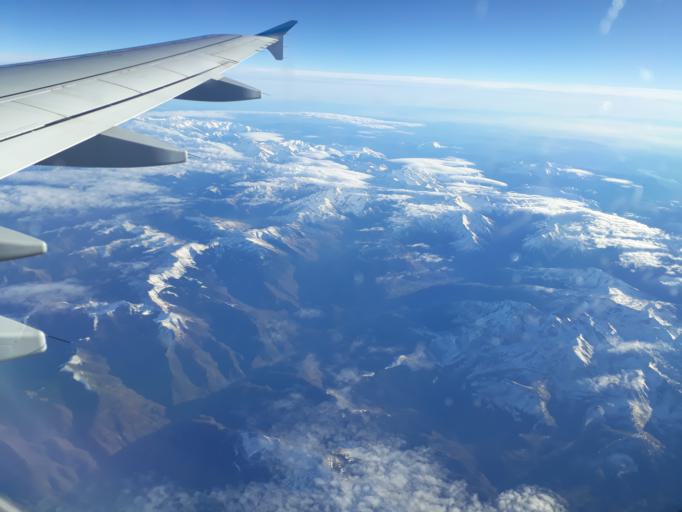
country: FR
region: Midi-Pyrenees
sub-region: Departement des Hautes-Pyrenees
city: Capvern
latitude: 43.0650
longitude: 0.2533
